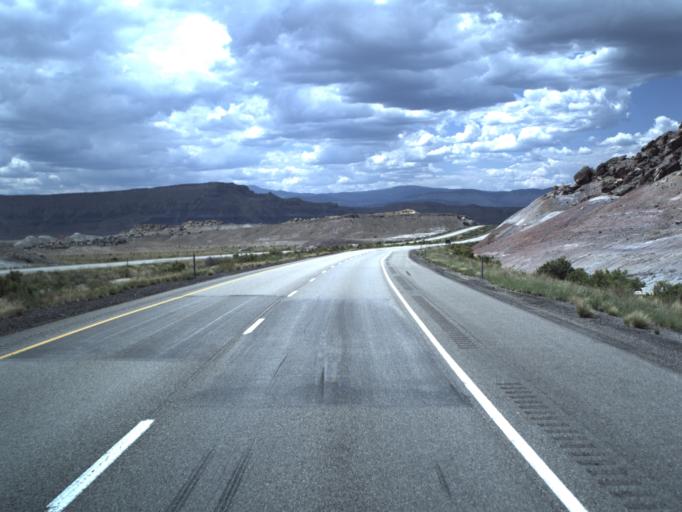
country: US
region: Utah
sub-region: Emery County
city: Ferron
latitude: 38.8191
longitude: -111.1572
